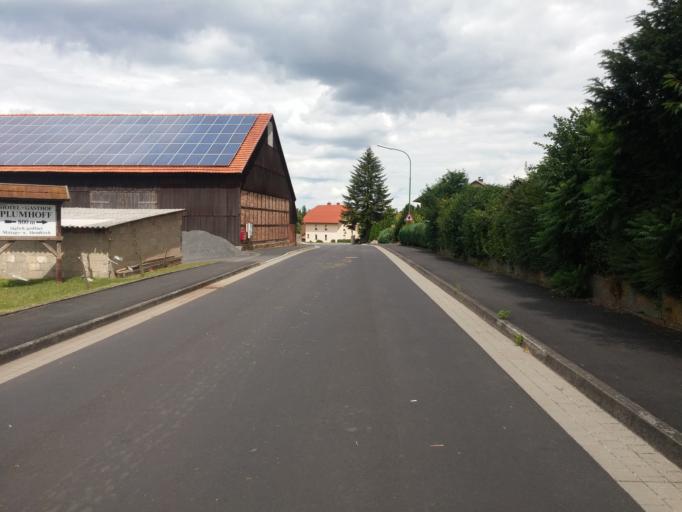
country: DE
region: Hesse
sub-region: Regierungsbezirk Kassel
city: Hunfeld
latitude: 50.6611
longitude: 9.7389
